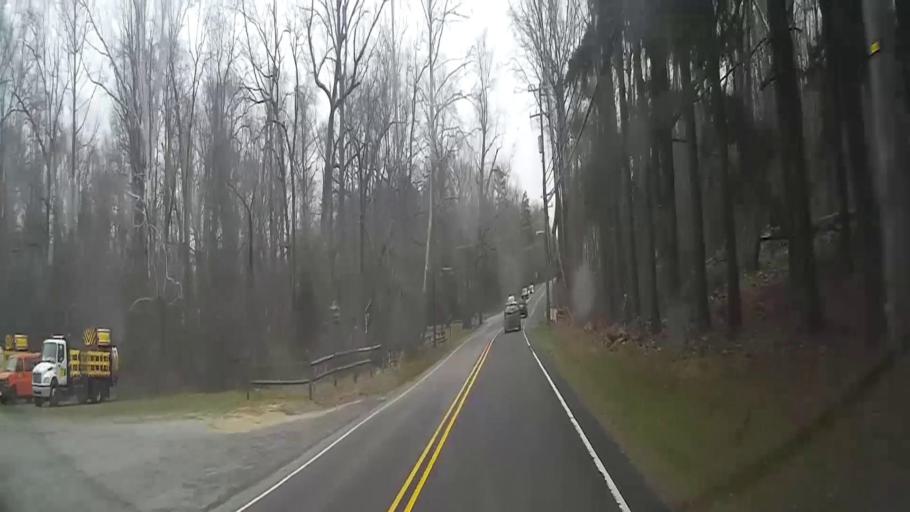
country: US
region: New Jersey
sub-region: Burlington County
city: Medford Lakes
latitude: 39.8789
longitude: -74.8606
